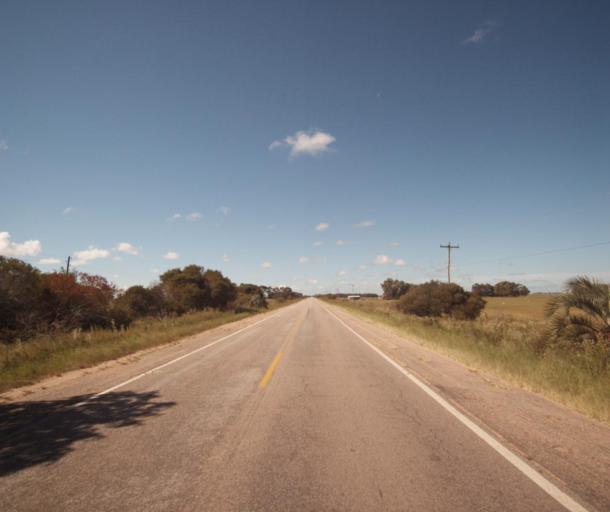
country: BR
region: Rio Grande do Sul
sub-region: Chui
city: Chui
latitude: -33.6391
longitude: -53.4208
